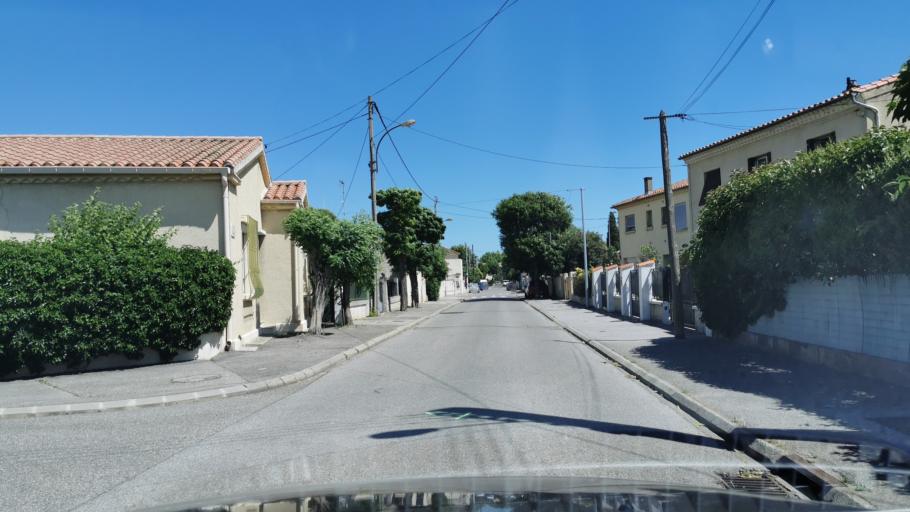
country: FR
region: Languedoc-Roussillon
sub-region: Departement de l'Aude
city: Narbonne
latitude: 43.1837
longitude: 2.9867
